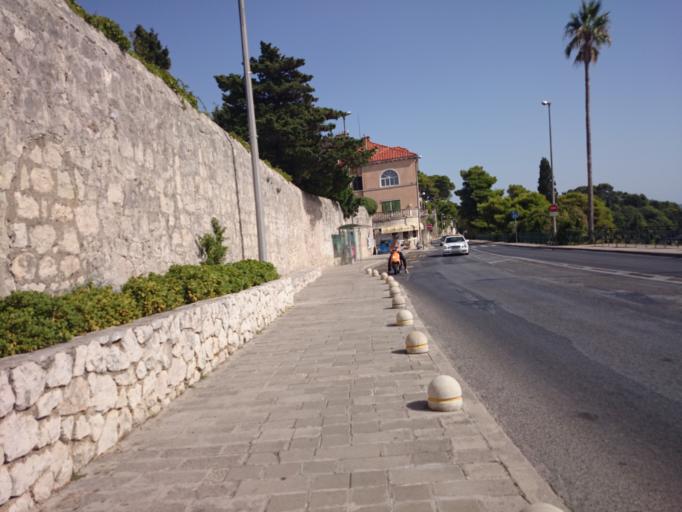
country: HR
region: Dubrovacko-Neretvanska
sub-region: Grad Dubrovnik
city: Dubrovnik
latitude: 42.6463
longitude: 18.0958
